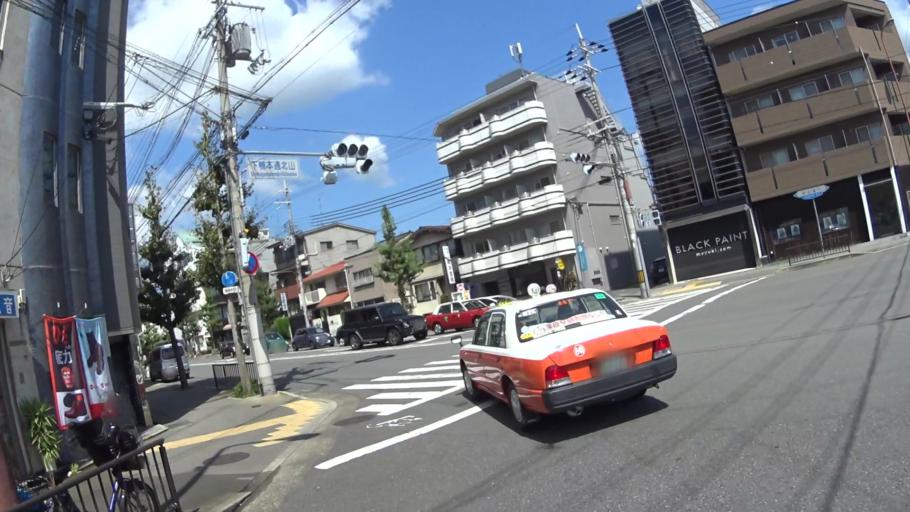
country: JP
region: Kyoto
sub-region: Kyoto-shi
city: Kamigyo-ku
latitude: 35.0513
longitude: 135.7704
